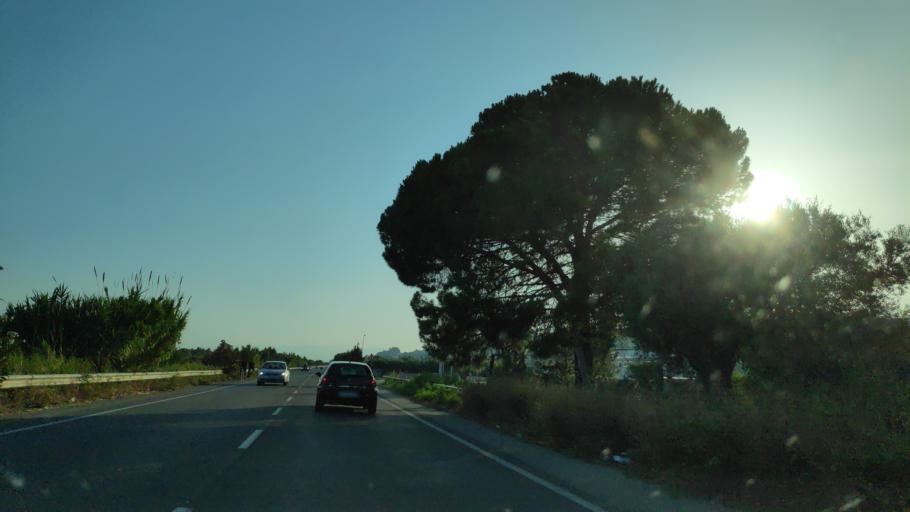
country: IT
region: Calabria
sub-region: Provincia di Reggio Calabria
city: Caulonia Marina
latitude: 38.3352
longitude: 16.4438
